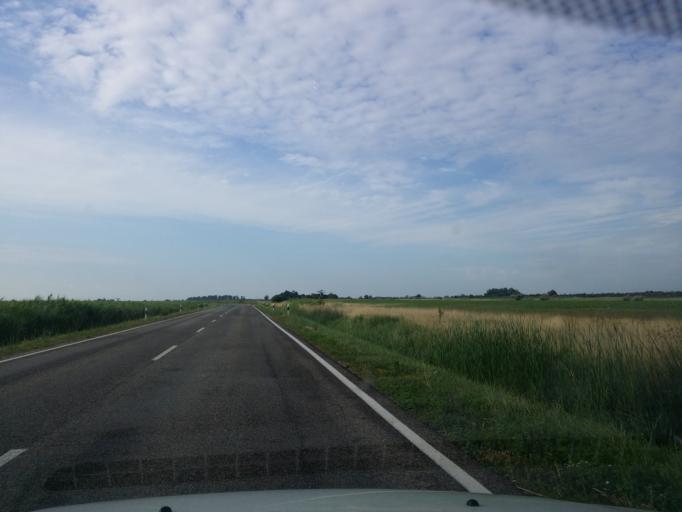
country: HU
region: Hajdu-Bihar
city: Egyek
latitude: 47.5617
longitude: 20.8635
